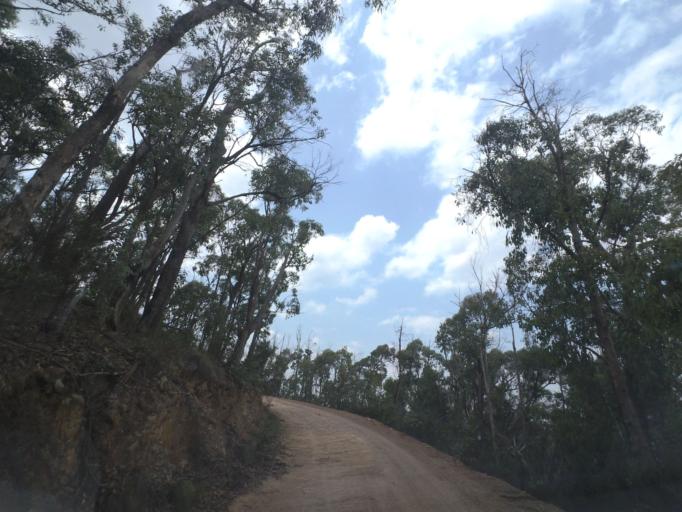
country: AU
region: Victoria
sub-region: Moorabool
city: Bacchus Marsh
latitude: -37.5615
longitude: 144.4260
